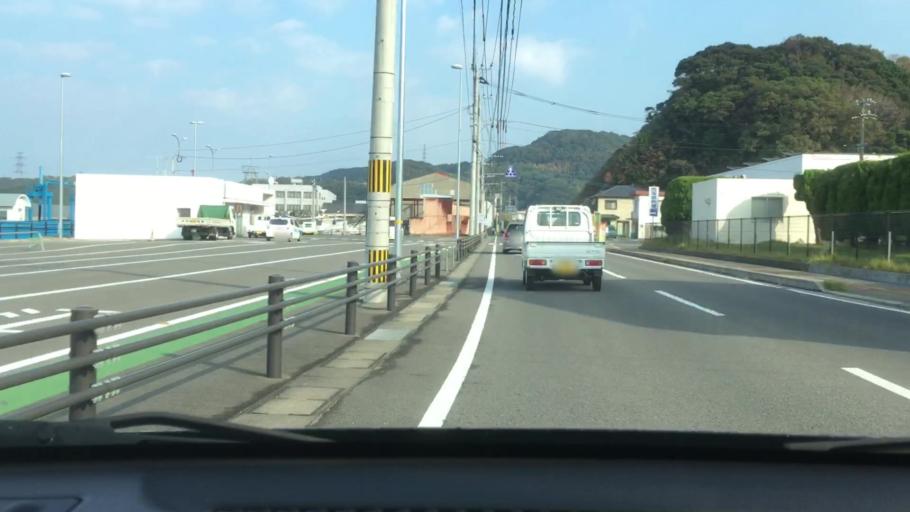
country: JP
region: Nagasaki
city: Sasebo
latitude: 32.9399
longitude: 129.6392
